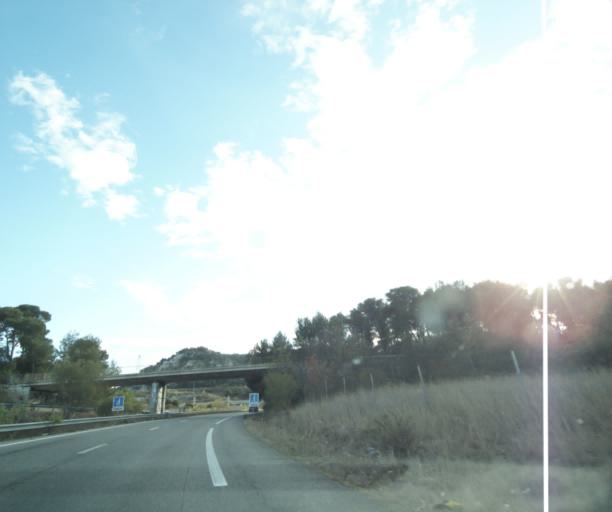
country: FR
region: Provence-Alpes-Cote d'Azur
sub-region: Departement des Bouches-du-Rhone
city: Les Pennes-Mirabeau
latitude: 43.4033
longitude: 5.2963
